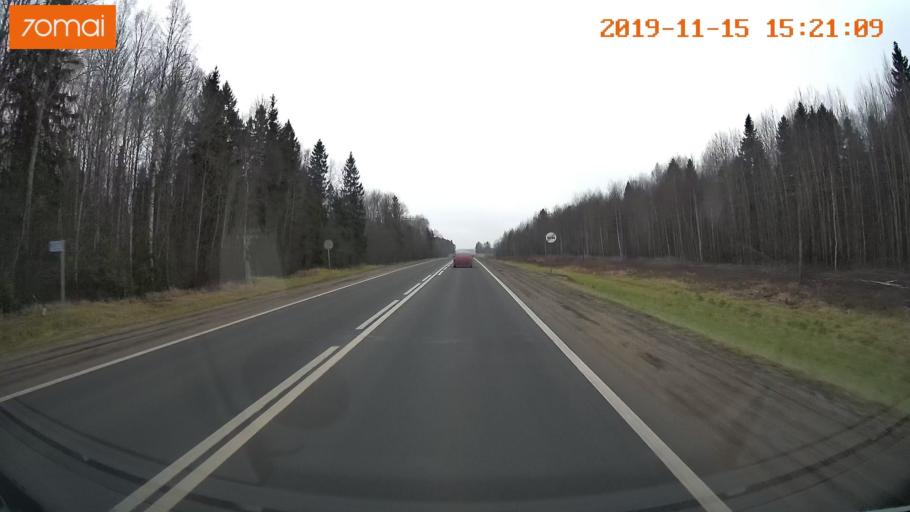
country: RU
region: Jaroslavl
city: Danilov
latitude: 58.2157
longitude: 40.1501
